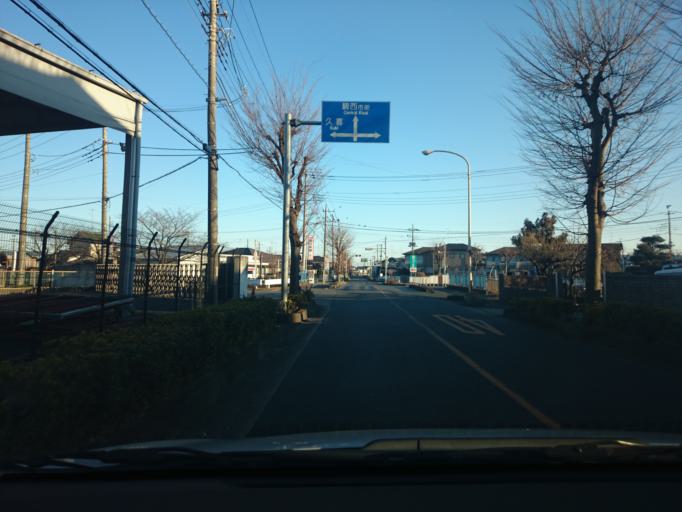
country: JP
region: Saitama
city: Kisai
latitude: 36.1111
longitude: 139.5664
